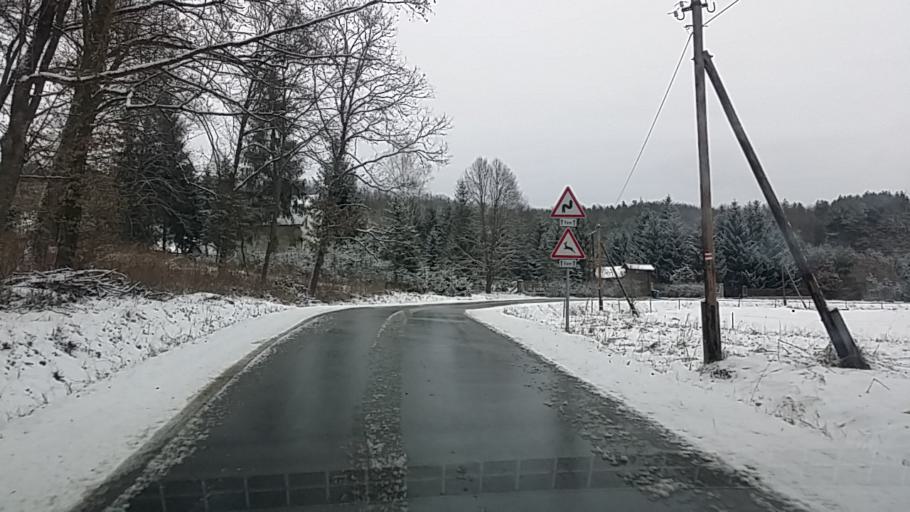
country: HU
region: Borsod-Abauj-Zemplen
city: Rudabanya
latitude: 48.4442
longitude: 20.6637
